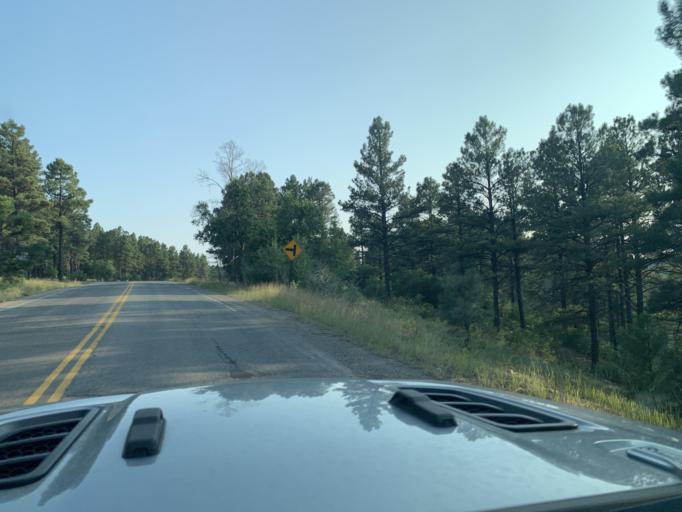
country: US
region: Colorado
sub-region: Archuleta County
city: Pagosa Springs
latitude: 37.2818
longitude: -107.0958
